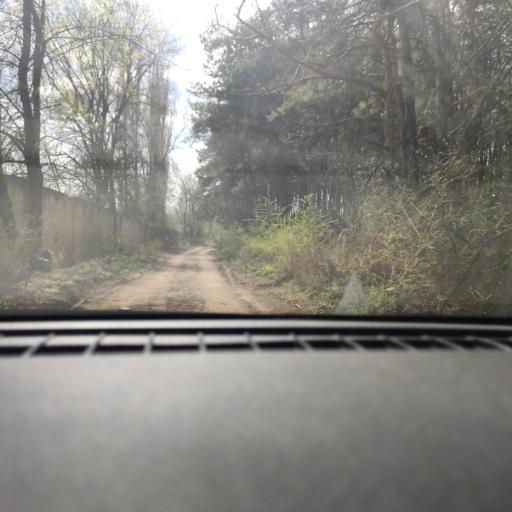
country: RU
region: Voronezj
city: Maslovka
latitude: 51.5966
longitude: 39.2190
